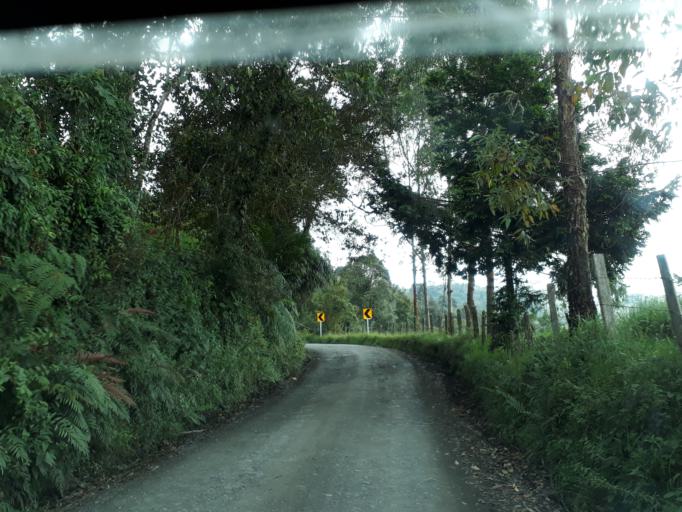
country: CO
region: Cundinamarca
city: Pacho
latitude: 5.2508
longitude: -74.1816
